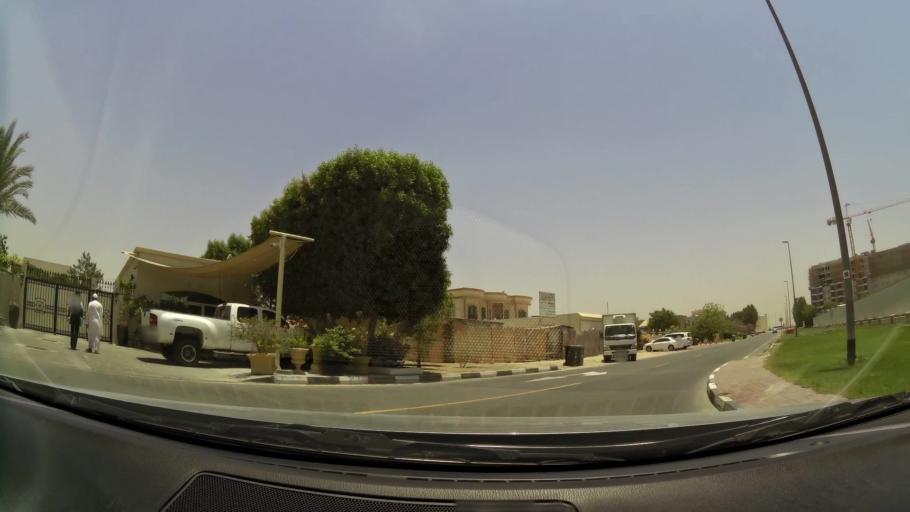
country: AE
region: Dubai
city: Dubai
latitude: 25.0972
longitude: 55.1863
